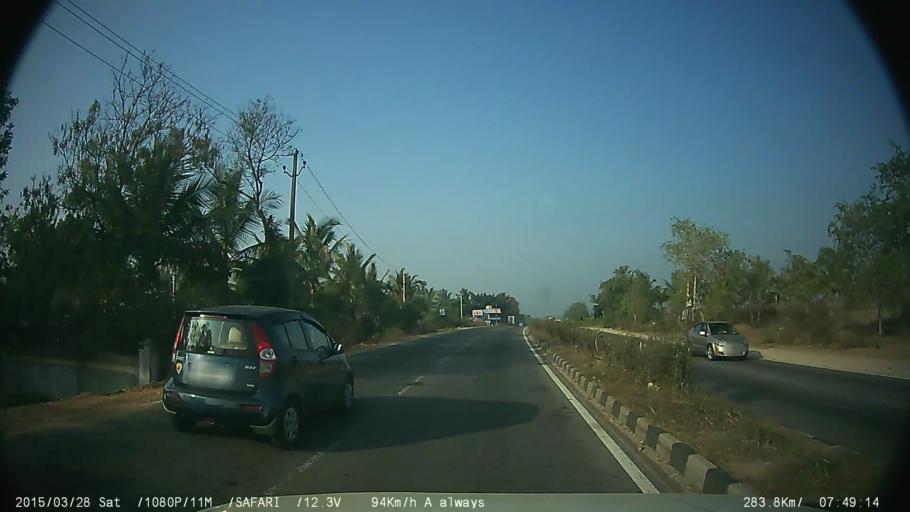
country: IN
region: Karnataka
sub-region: Mandya
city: Pandavapura
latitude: 12.4741
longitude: 76.7620
